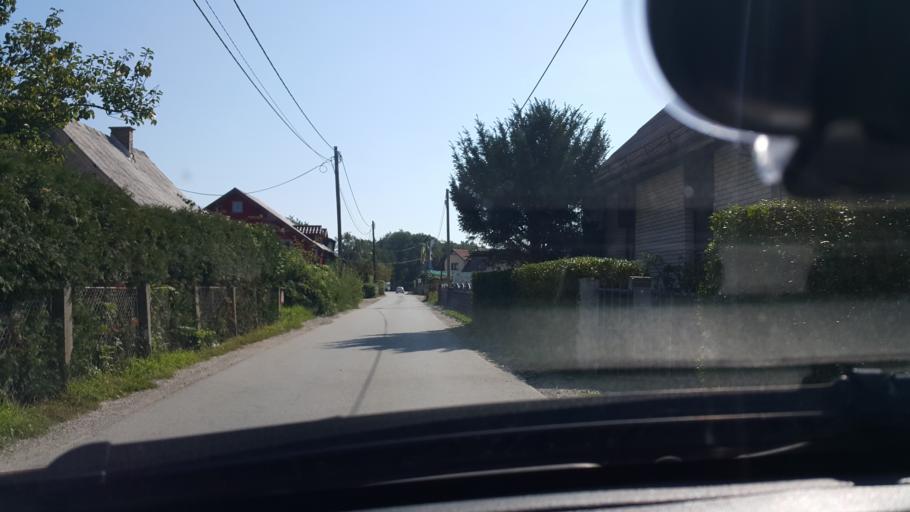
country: SI
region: Maribor
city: Maribor
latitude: 46.5308
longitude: 15.6616
